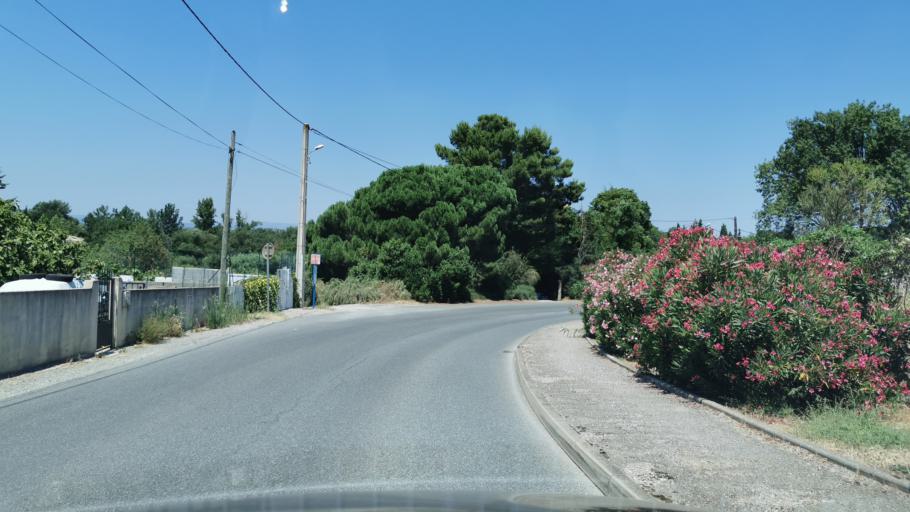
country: FR
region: Languedoc-Roussillon
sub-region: Departement de l'Herault
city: Maureilhan
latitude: 43.3605
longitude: 3.1181
